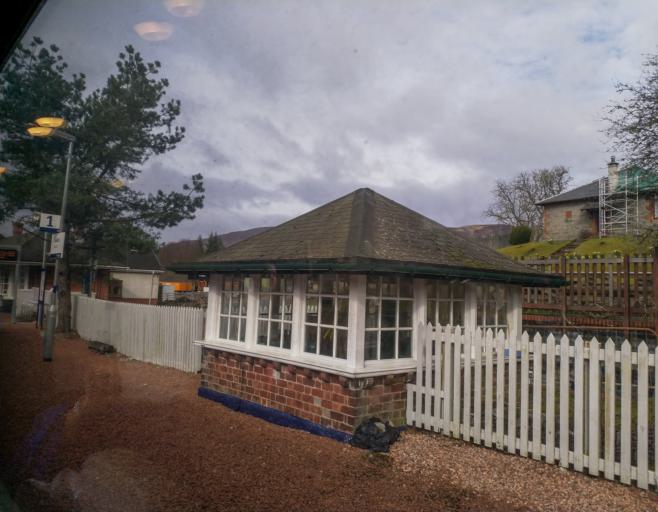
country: GB
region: Scotland
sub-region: Highland
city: Spean Bridge
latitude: 56.8841
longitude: -4.7009
